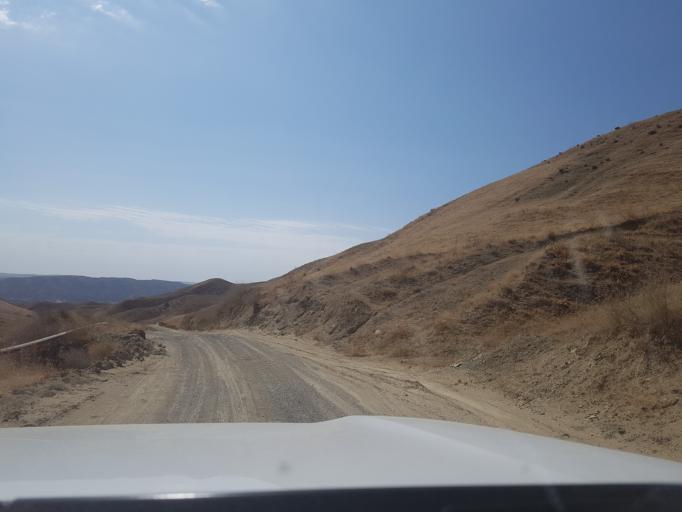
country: TM
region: Ahal
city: Baharly
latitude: 38.2610
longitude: 56.8885
